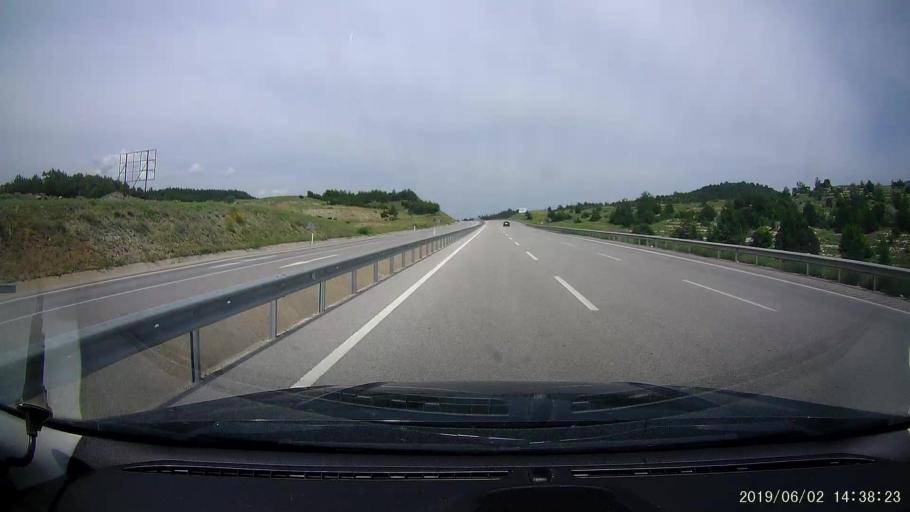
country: TR
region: Corum
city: Hacihamza
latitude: 41.0544
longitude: 34.2795
